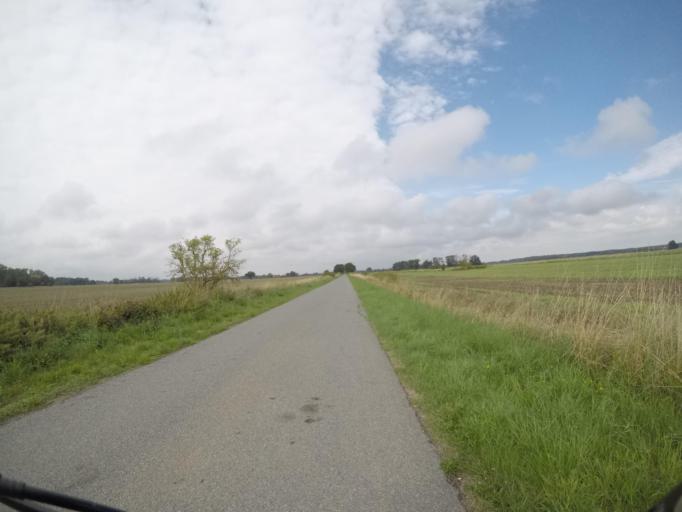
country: DE
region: Lower Saxony
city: Neu Darchau
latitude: 53.2878
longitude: 10.9067
